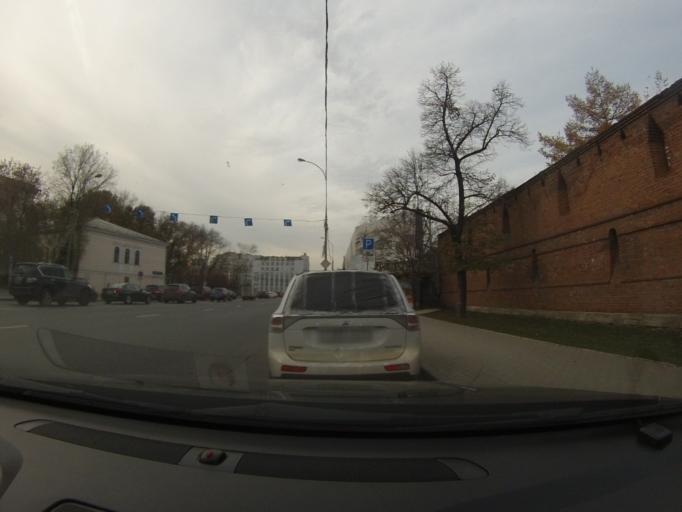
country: RU
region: Moscow
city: Moscow
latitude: 55.7509
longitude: 37.6327
